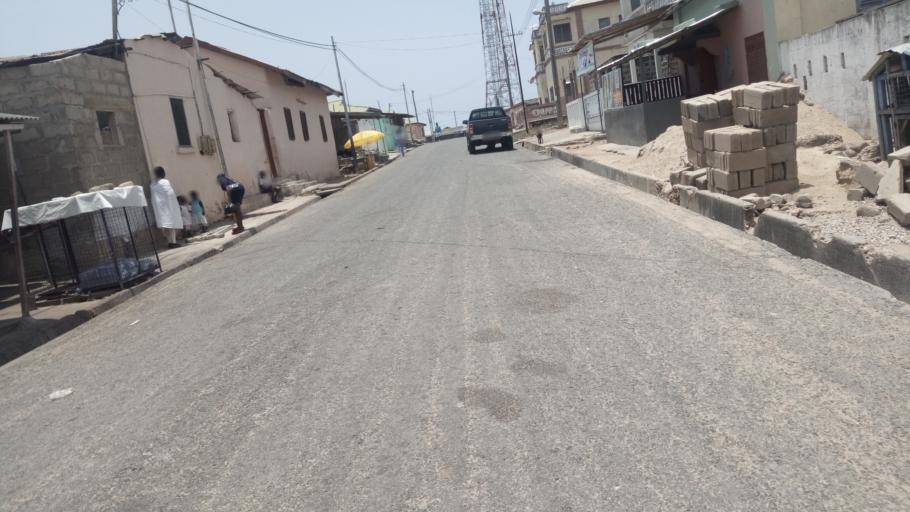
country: GH
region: Central
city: Winneba
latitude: 5.3451
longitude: -0.6244
